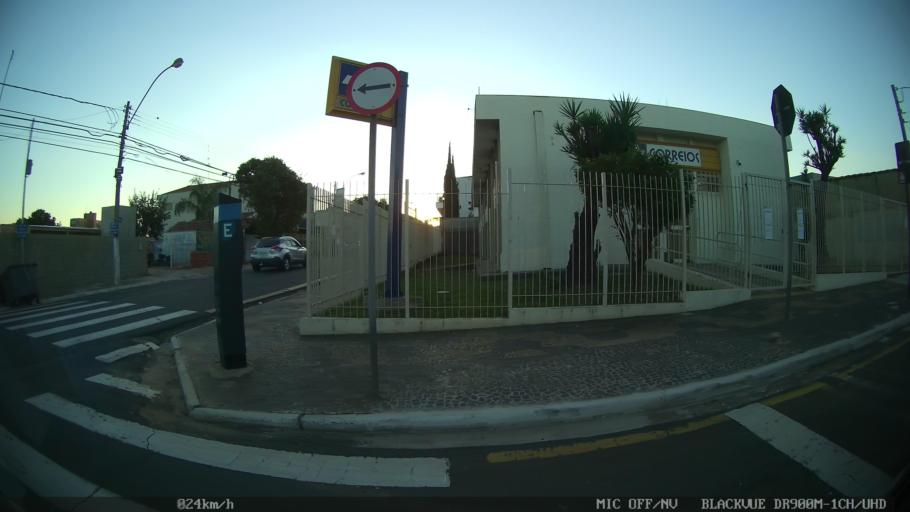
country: BR
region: Sao Paulo
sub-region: Santa Barbara D'Oeste
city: Santa Barbara d'Oeste
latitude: -22.7572
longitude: -47.4154
